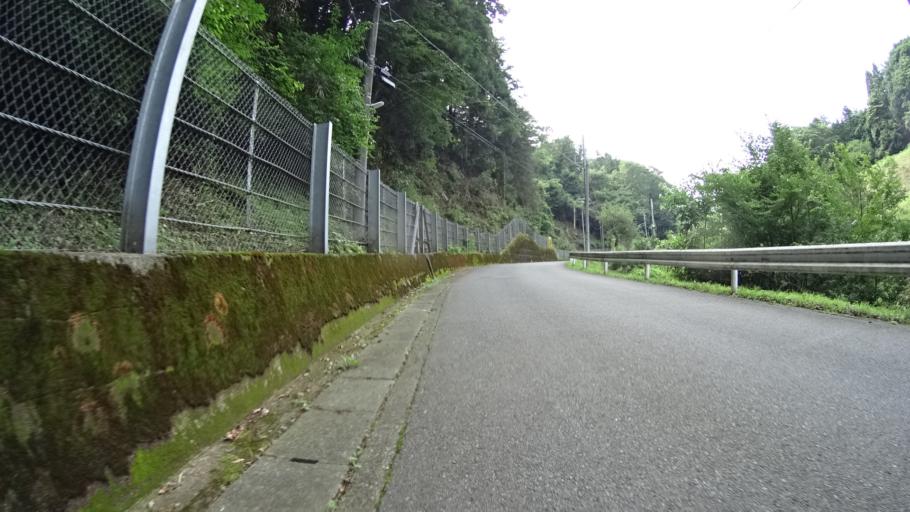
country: JP
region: Kanagawa
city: Atsugi
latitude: 35.4933
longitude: 139.2702
